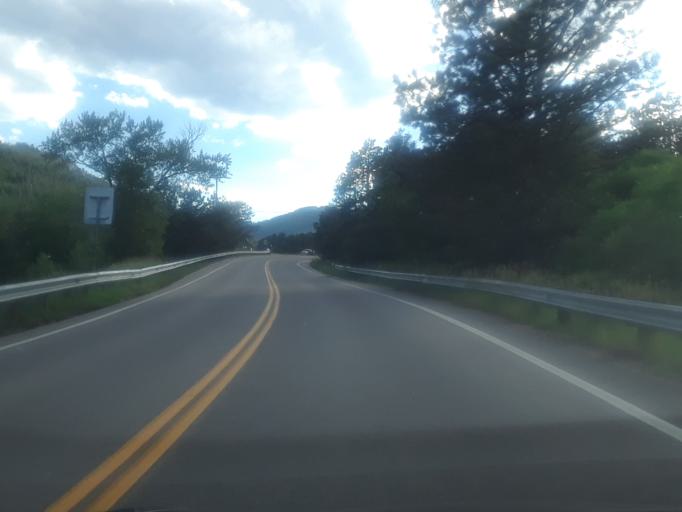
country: US
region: Colorado
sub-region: Jefferson County
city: Kittredge
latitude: 39.7172
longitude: -105.3897
